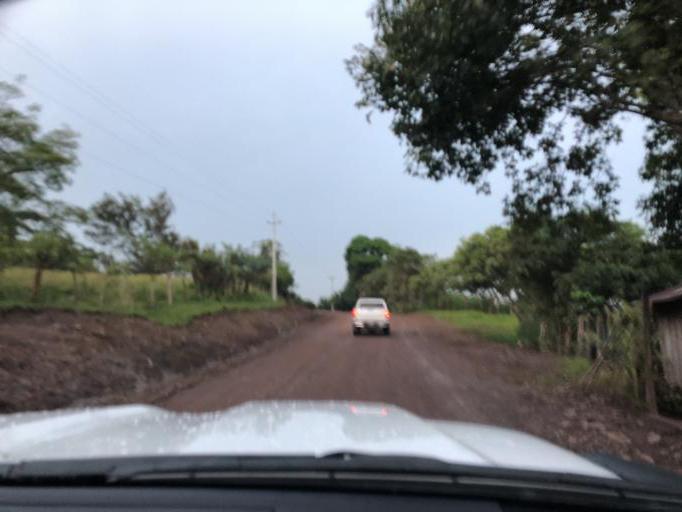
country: NI
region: Chontales
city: La Libertad
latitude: 12.1770
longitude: -85.1733
